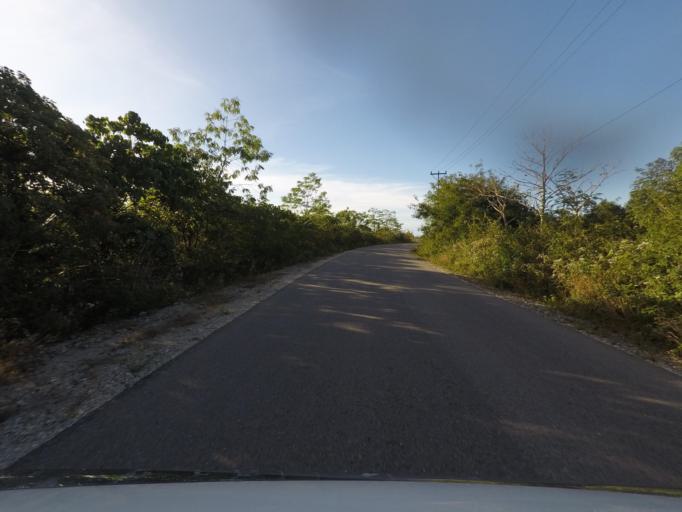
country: TL
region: Lautem
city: Lospalos
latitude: -8.3831
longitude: 127.0138
